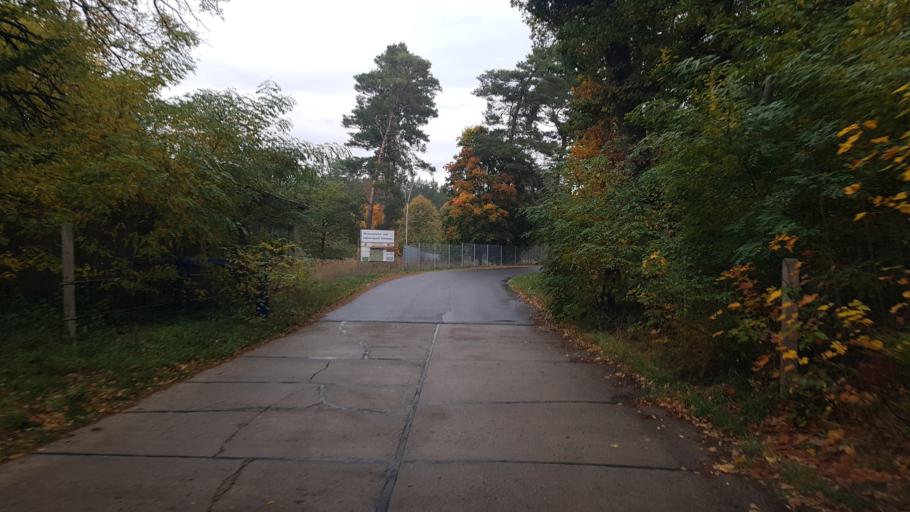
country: DE
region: Brandenburg
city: Schlieben
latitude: 51.7422
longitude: 13.3799
